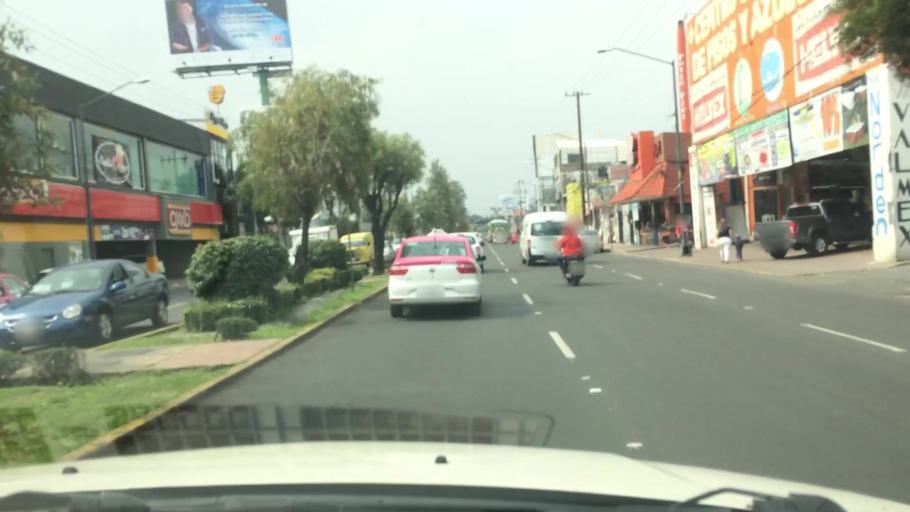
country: MX
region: Mexico City
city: Xochimilco
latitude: 19.2771
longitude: -99.1218
